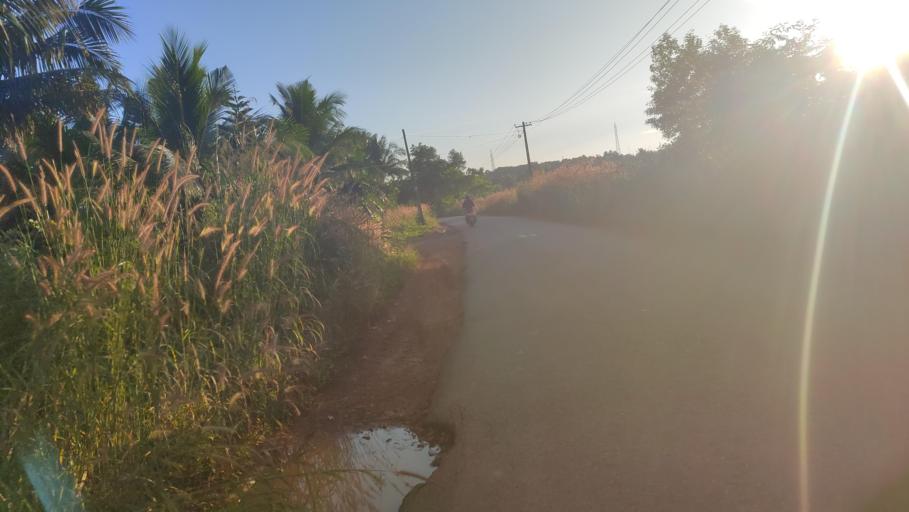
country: IN
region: Kerala
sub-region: Kasaragod District
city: Kannangad
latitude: 12.4154
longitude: 75.0954
